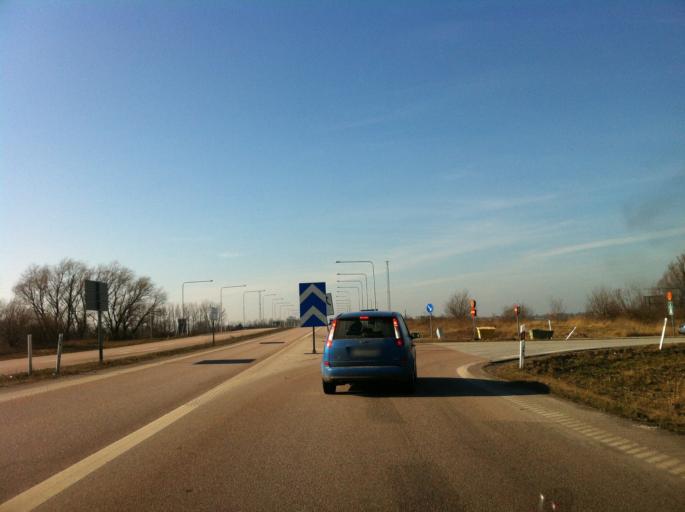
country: SE
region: Skane
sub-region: Landskrona
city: Asmundtorp
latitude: 55.8759
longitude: 12.8836
